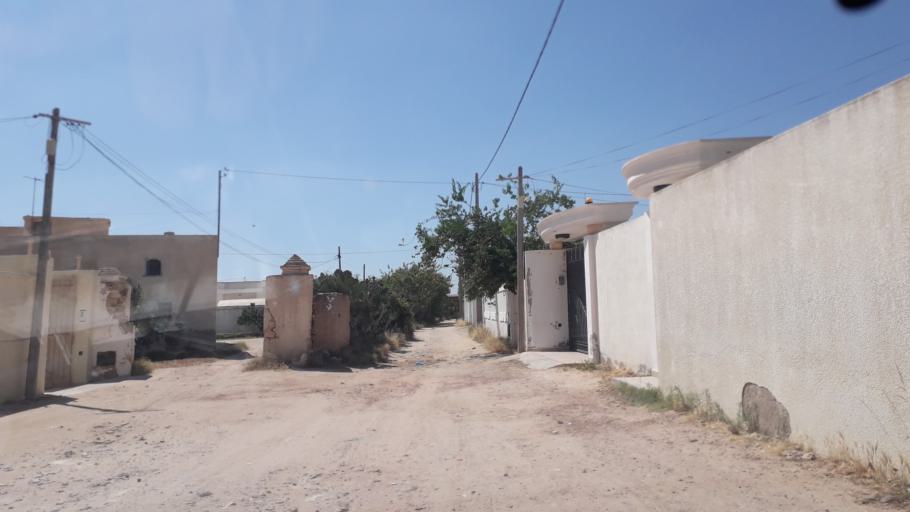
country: TN
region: Safaqis
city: Al Qarmadah
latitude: 34.8186
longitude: 10.7640
